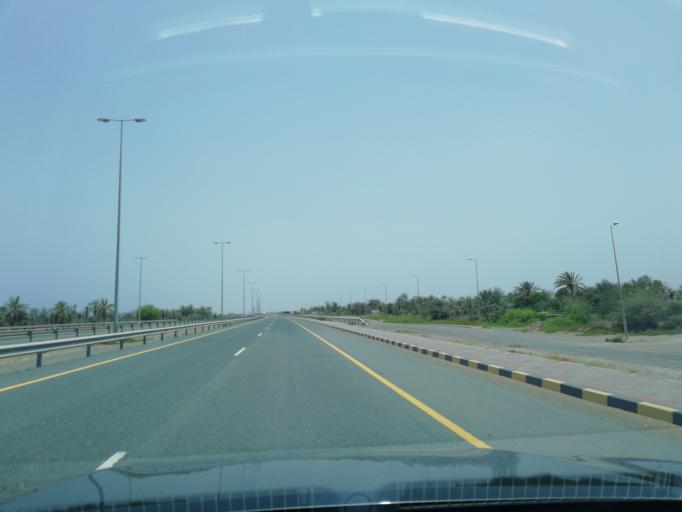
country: OM
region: Al Batinah
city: Shinas
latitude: 24.7744
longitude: 56.4584
